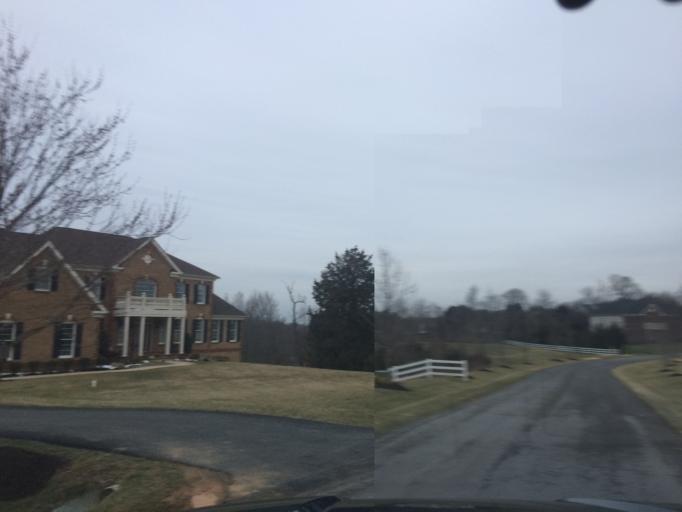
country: US
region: Maryland
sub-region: Howard County
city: Highland
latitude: 39.2667
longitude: -77.0033
